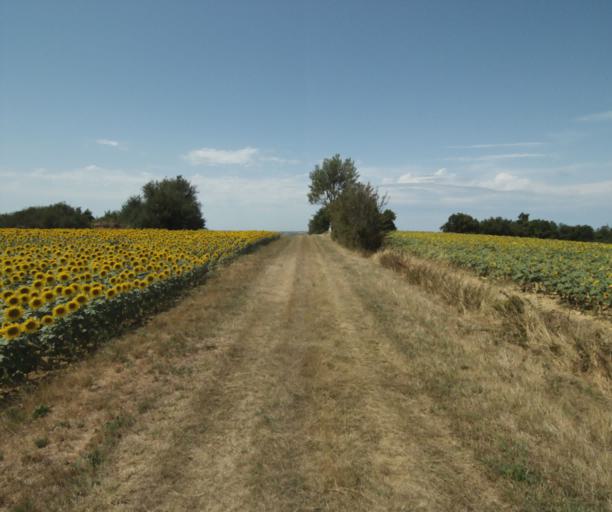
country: FR
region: Midi-Pyrenees
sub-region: Departement de la Haute-Garonne
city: Saint-Felix-Lauragais
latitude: 43.4477
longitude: 1.8604
